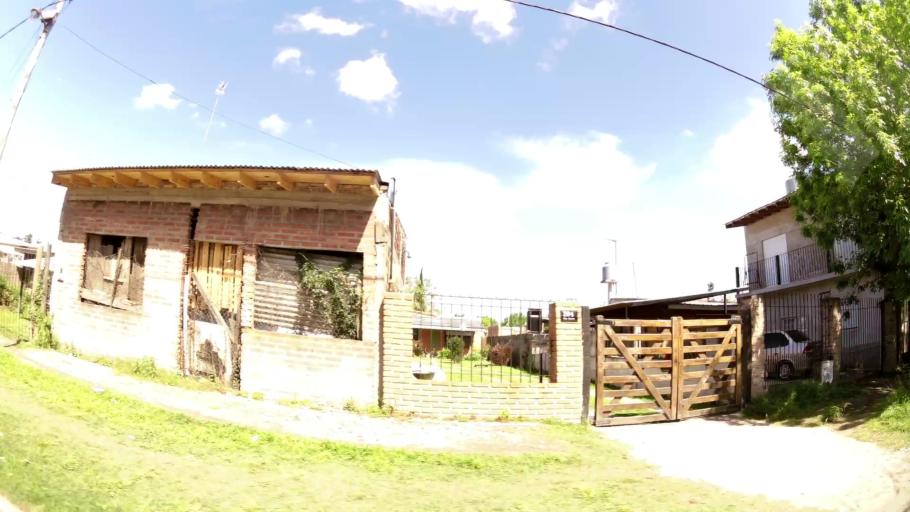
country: AR
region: Buenos Aires
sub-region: Partido de Quilmes
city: Quilmes
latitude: -34.8206
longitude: -58.2655
